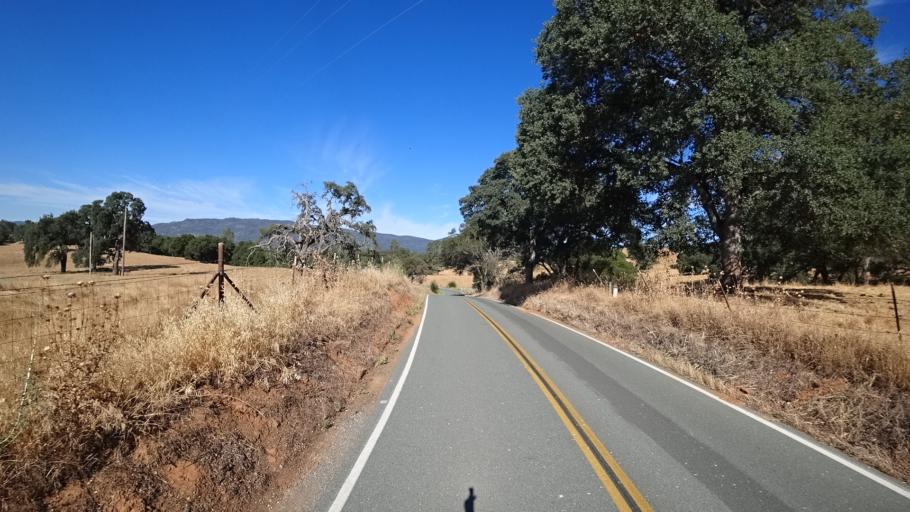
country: US
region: California
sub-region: Calaveras County
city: San Andreas
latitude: 38.1714
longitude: -120.6327
